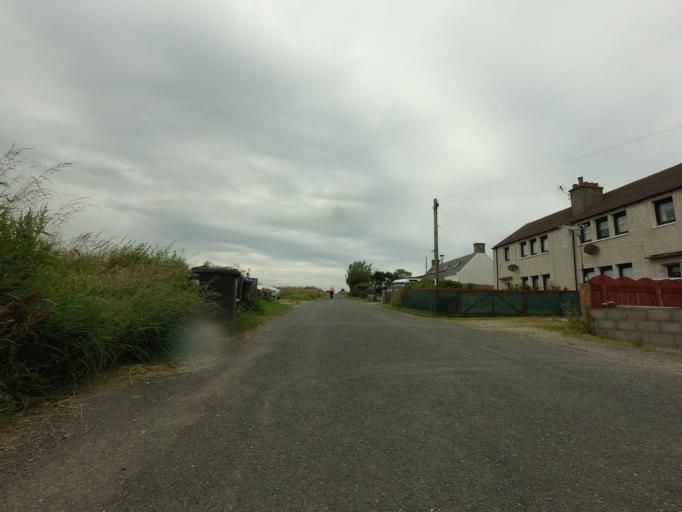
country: GB
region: Scotland
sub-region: Aberdeenshire
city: Portsoy
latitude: 57.6777
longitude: -2.6696
